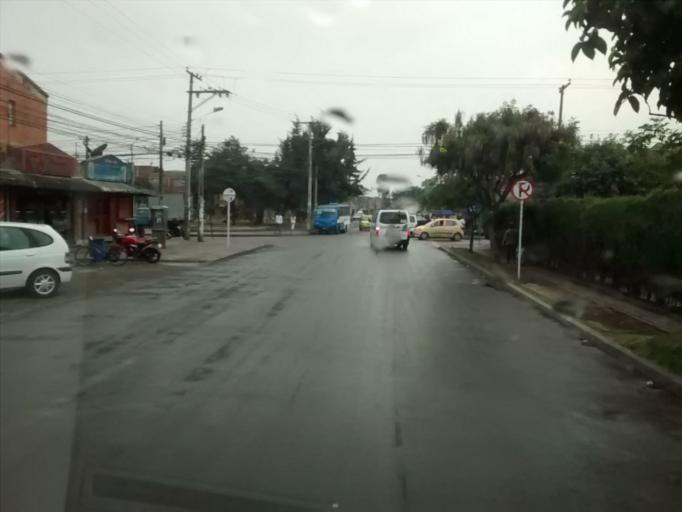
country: CO
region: Cundinamarca
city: Cota
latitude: 4.7561
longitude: -74.1031
